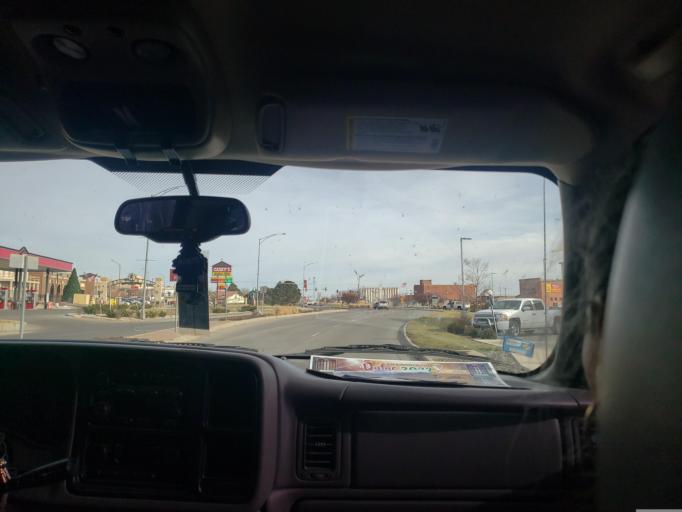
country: US
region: Kansas
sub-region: Ford County
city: Dodge City
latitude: 37.7531
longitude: -100.0238
